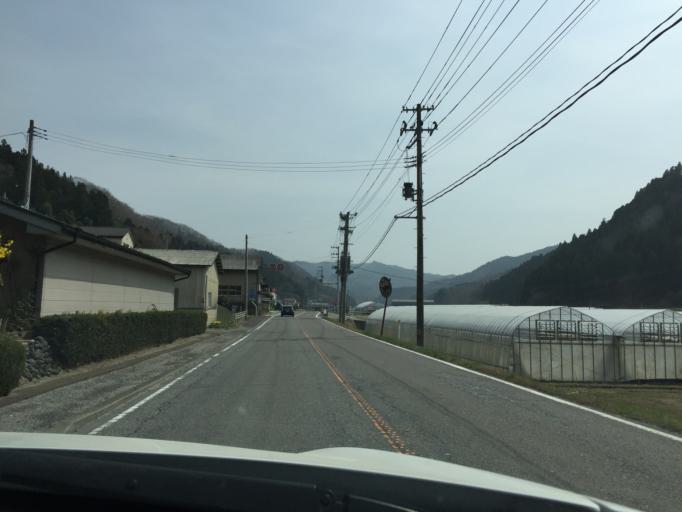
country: JP
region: Fukushima
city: Ishikawa
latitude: 37.1004
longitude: 140.5103
